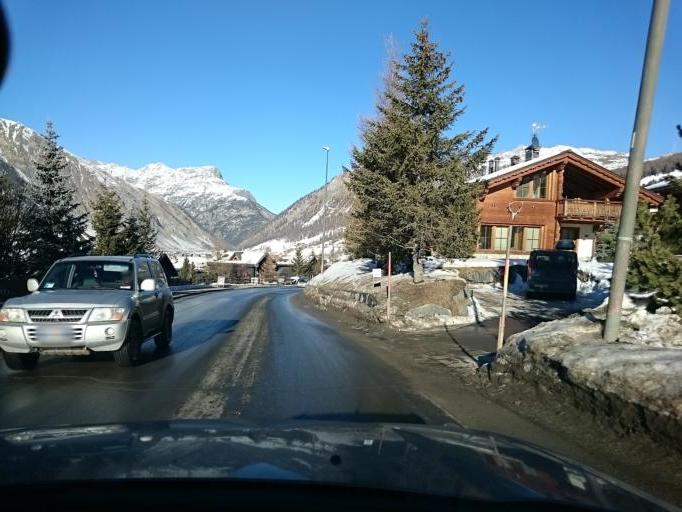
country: IT
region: Lombardy
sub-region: Provincia di Sondrio
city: Livigno
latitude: 46.5308
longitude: 10.1379
